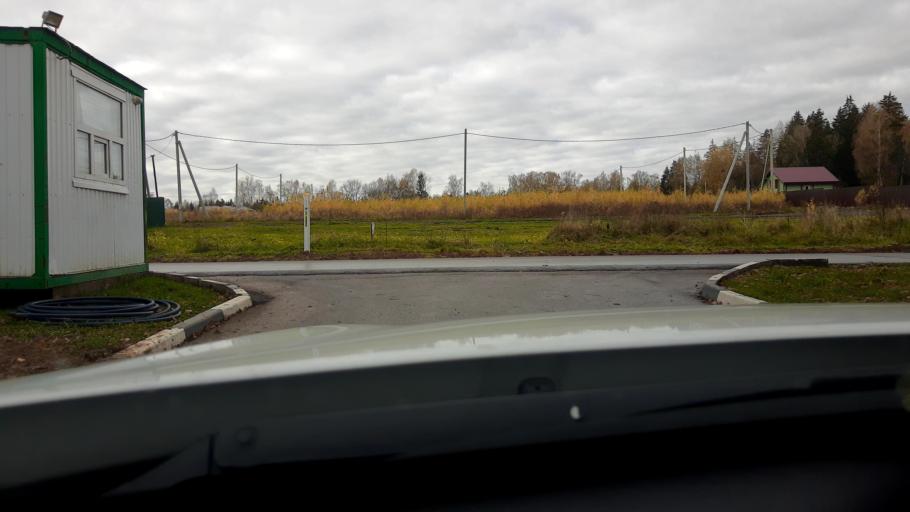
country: RU
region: Moskovskaya
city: Annino
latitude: 55.5605
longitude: 37.2525
